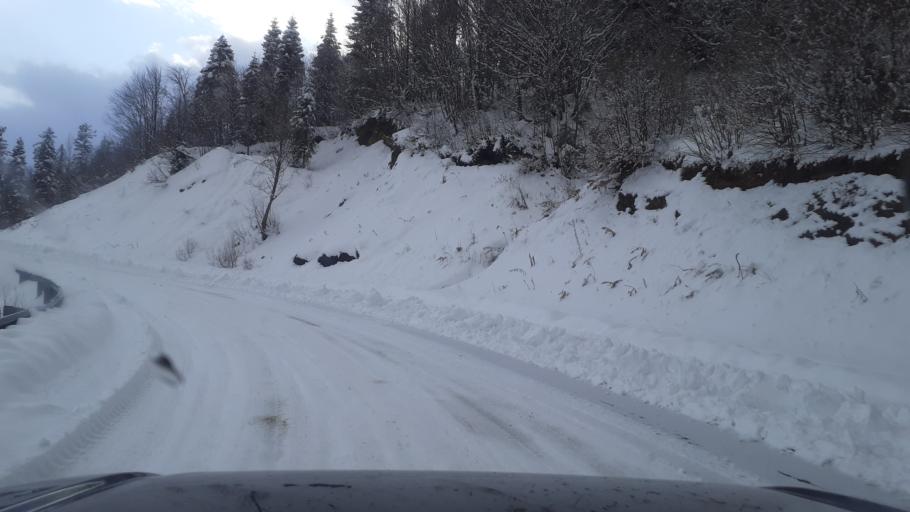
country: RU
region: Adygeya
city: Kamennomostskiy
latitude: 44.0114
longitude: 40.0037
